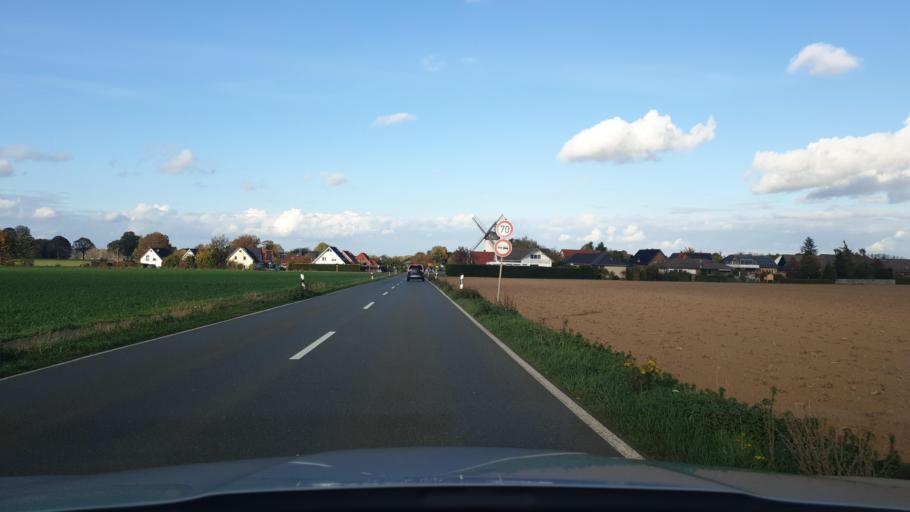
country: DE
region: North Rhine-Westphalia
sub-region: Regierungsbezirk Detmold
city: Minden
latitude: 52.2692
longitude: 8.8516
